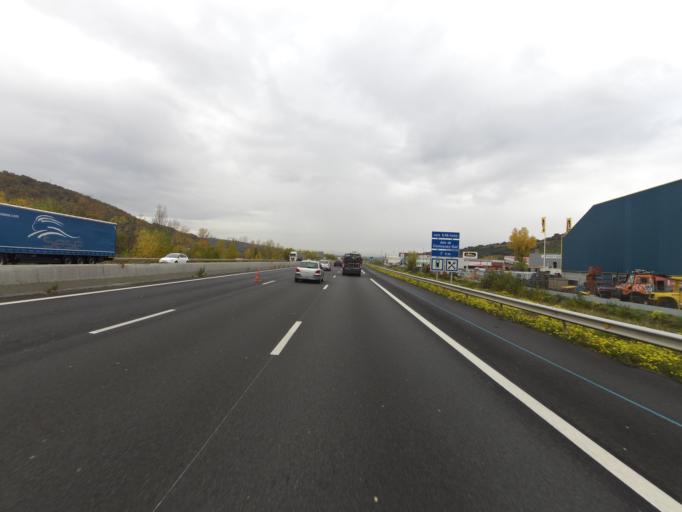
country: FR
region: Rhone-Alpes
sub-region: Departement de l'Isere
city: Seyssuel
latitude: 45.5488
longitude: 4.8335
